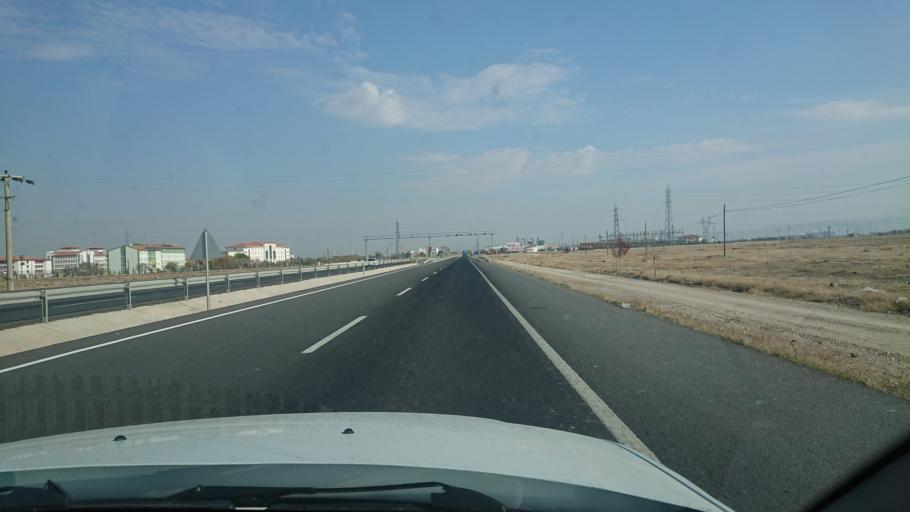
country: TR
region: Aksaray
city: Aksaray
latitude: 38.3401
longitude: 33.9449
